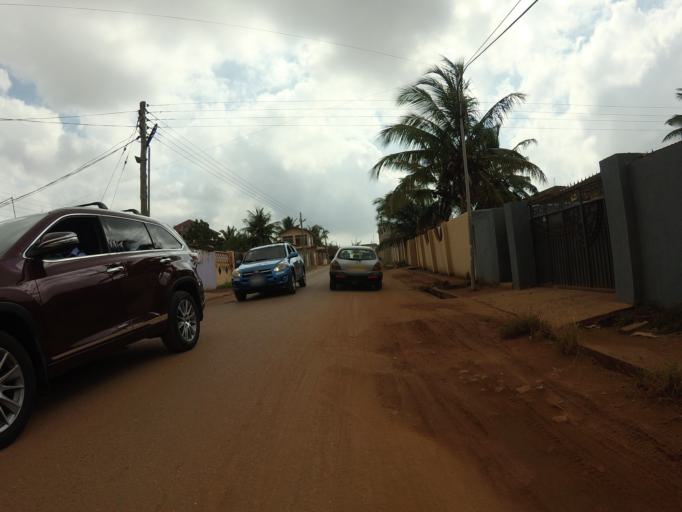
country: GH
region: Greater Accra
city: Nungua
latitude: 5.6190
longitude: -0.1009
